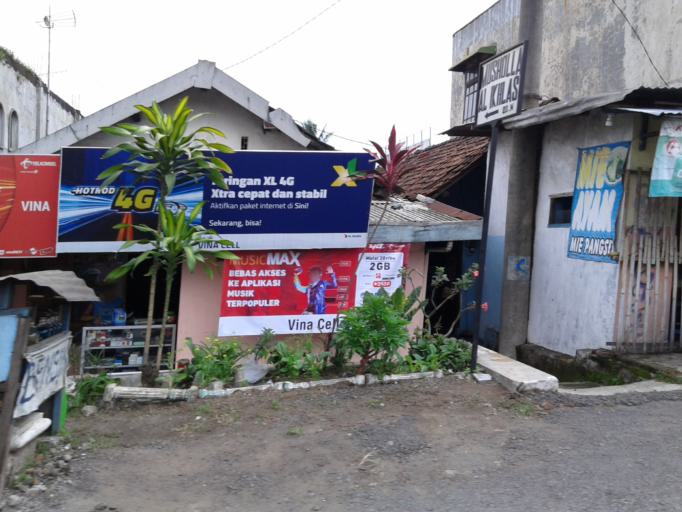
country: ID
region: East Java
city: Lawang
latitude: -7.8590
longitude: 112.6883
